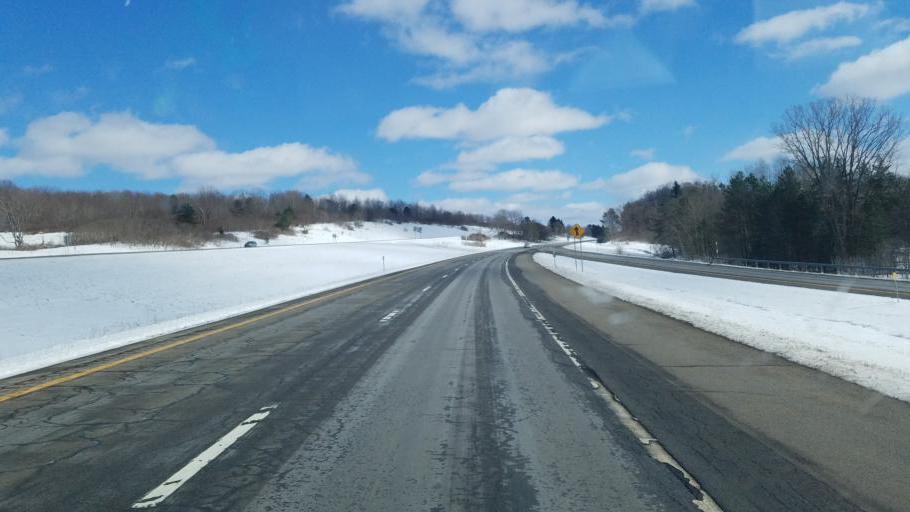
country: US
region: New York
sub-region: Chautauqua County
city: Celoron
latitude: 42.1246
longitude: -79.2711
